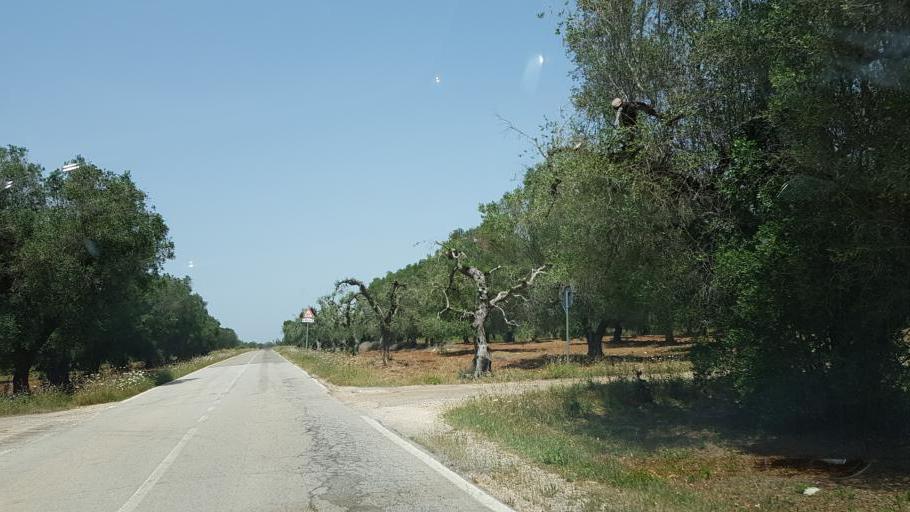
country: IT
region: Apulia
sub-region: Provincia di Brindisi
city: San Pancrazio Salentino
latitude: 40.4592
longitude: 17.8394
